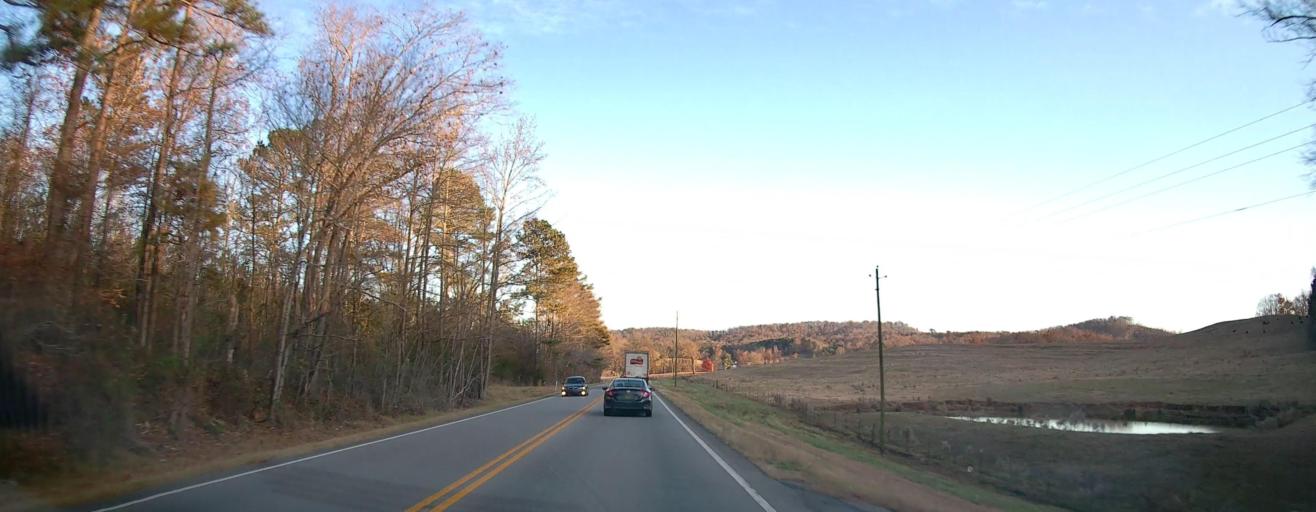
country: US
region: Alabama
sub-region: Saint Clair County
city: Steele
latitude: 34.0749
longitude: -86.3322
